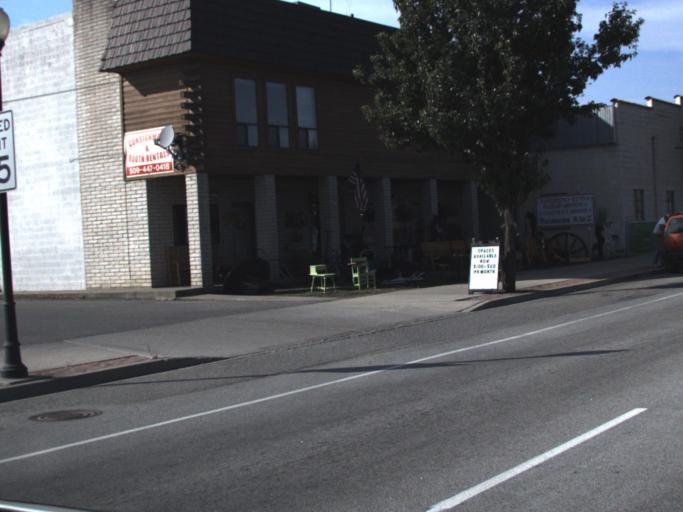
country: US
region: Washington
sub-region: Pend Oreille County
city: Newport
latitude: 48.1786
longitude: -117.0425
